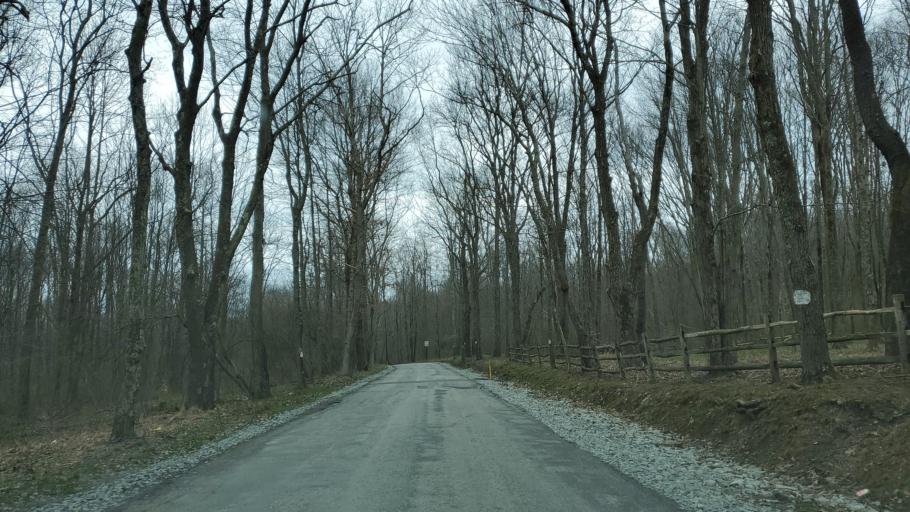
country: US
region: Pennsylvania
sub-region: Westmoreland County
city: Ligonier
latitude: 40.1699
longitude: -79.2628
